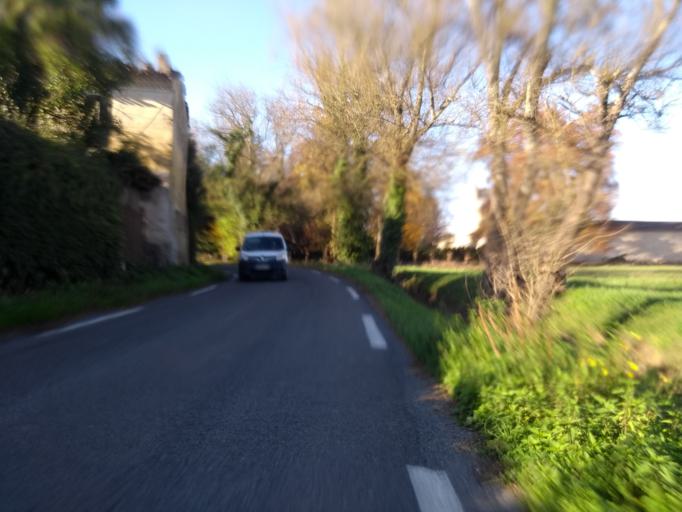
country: FR
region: Aquitaine
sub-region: Departement de la Gironde
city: Ayguemorte-les-Graves
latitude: 44.7259
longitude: -0.4879
